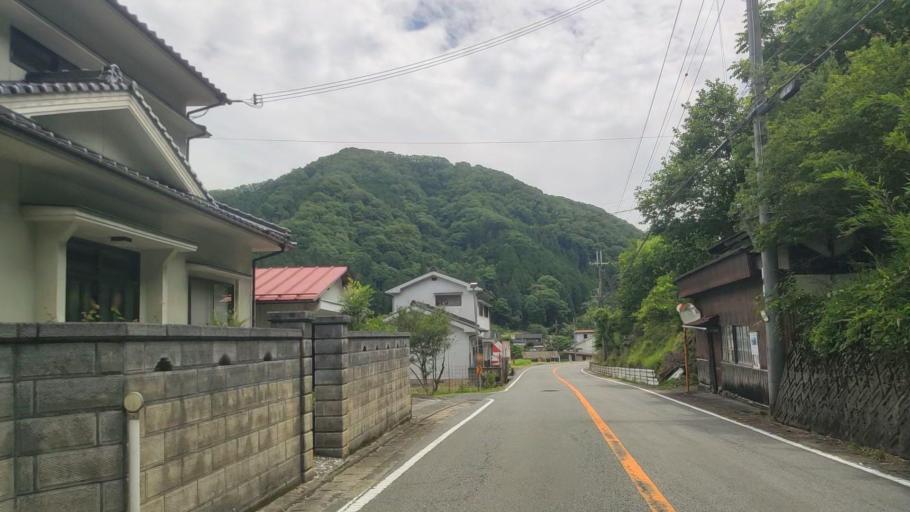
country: JP
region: Hyogo
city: Yamazakicho-nakabirose
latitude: 35.1021
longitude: 134.3626
